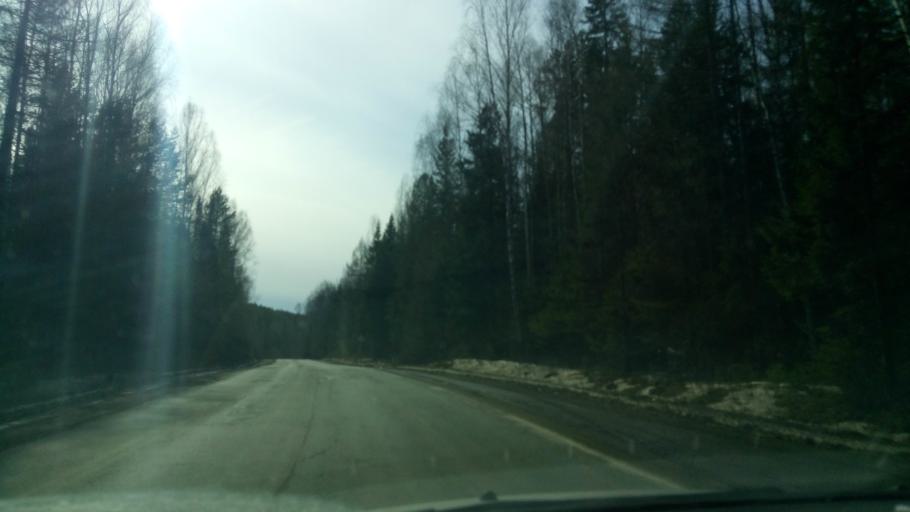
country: RU
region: Sverdlovsk
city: Chernoistochinsk
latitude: 57.7312
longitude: 59.7867
